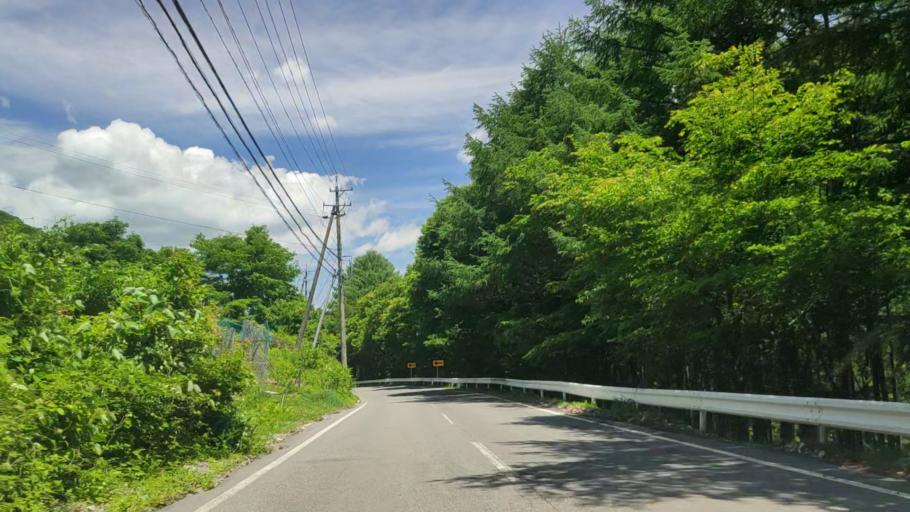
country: JP
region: Nagano
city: Kamimaruko
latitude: 36.1638
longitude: 138.2397
